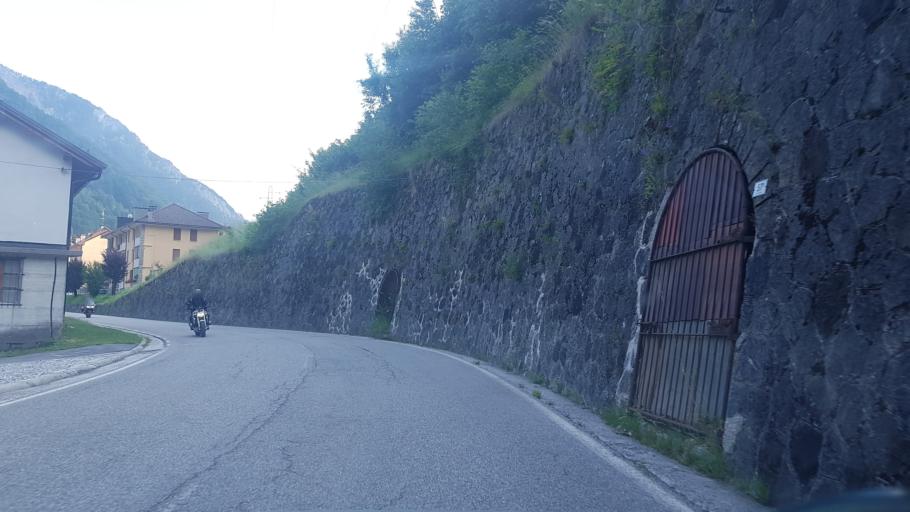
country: IT
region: Friuli Venezia Giulia
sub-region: Provincia di Udine
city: Pontebba
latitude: 46.5077
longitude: 13.3019
